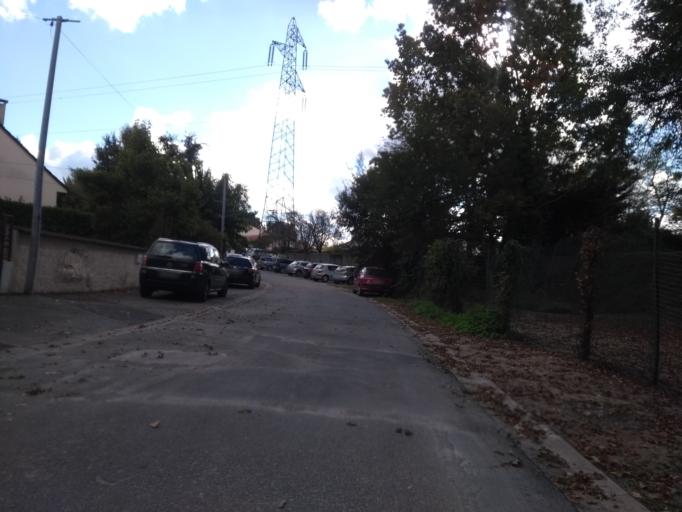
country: FR
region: Aquitaine
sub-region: Departement de la Gironde
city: Canejan
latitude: 44.7593
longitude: -0.6389
